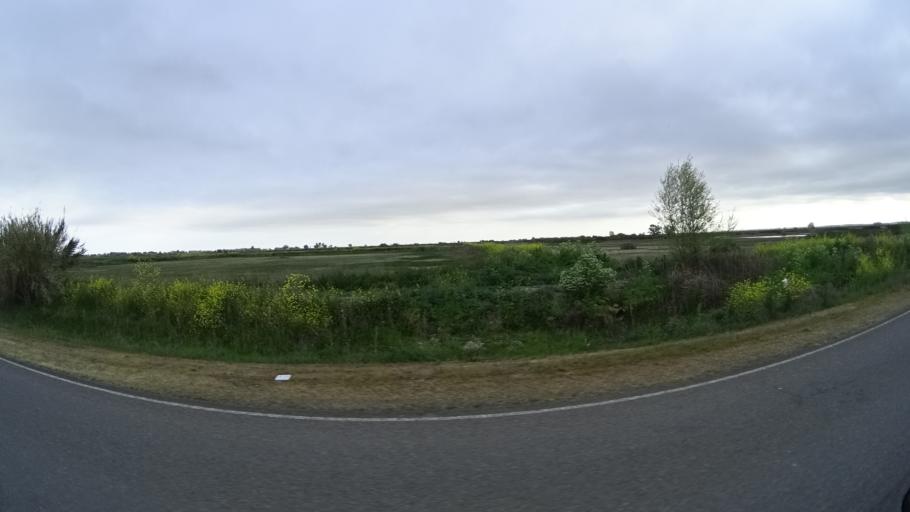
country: US
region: California
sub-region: Glenn County
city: Willows
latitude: 39.4065
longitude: -122.0935
